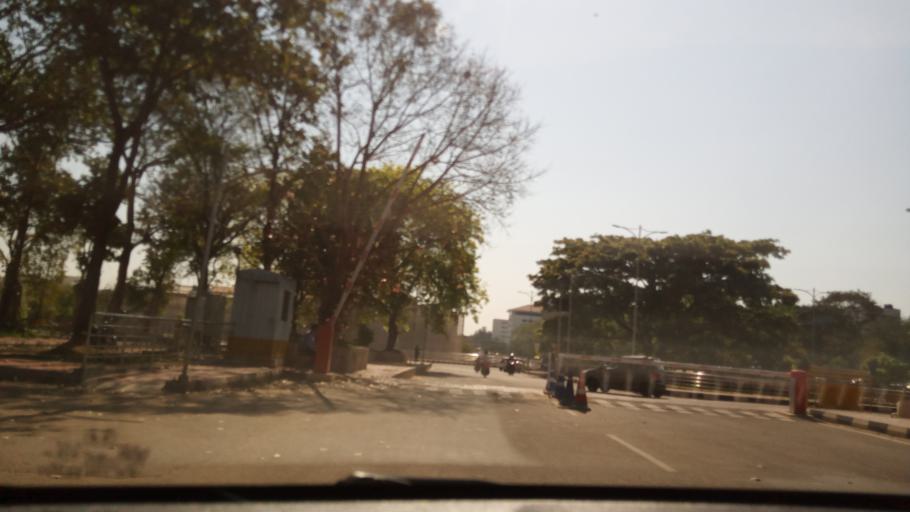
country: IN
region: Karnataka
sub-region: Bangalore Urban
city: Bangalore
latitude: 13.0294
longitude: 77.5660
